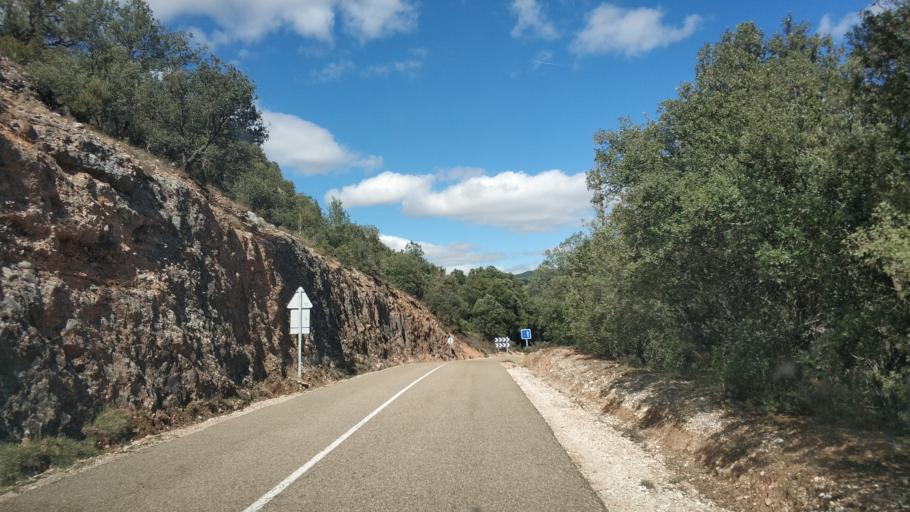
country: ES
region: Castille and Leon
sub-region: Provincia de Burgos
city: Retuerta
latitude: 42.0377
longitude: -3.4806
